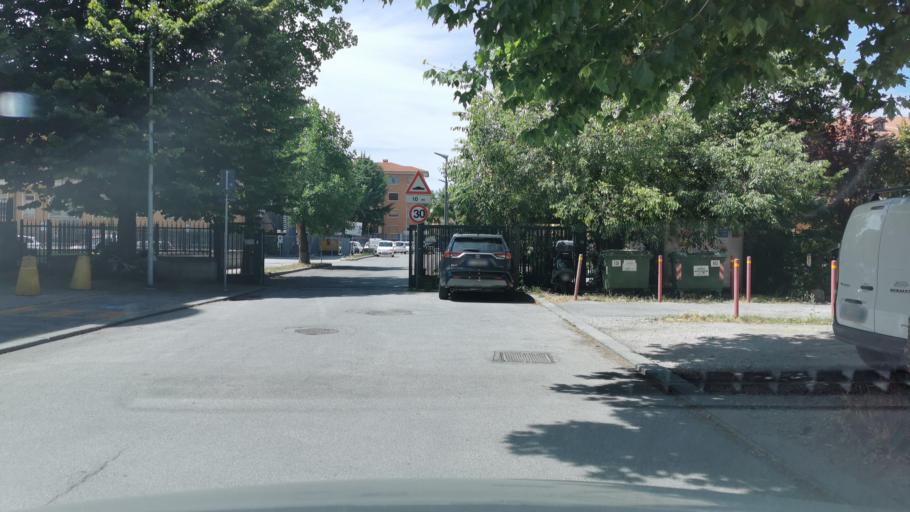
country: IT
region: Piedmont
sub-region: Provincia di Cuneo
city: Cuneo
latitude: 44.3761
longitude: 7.5328
